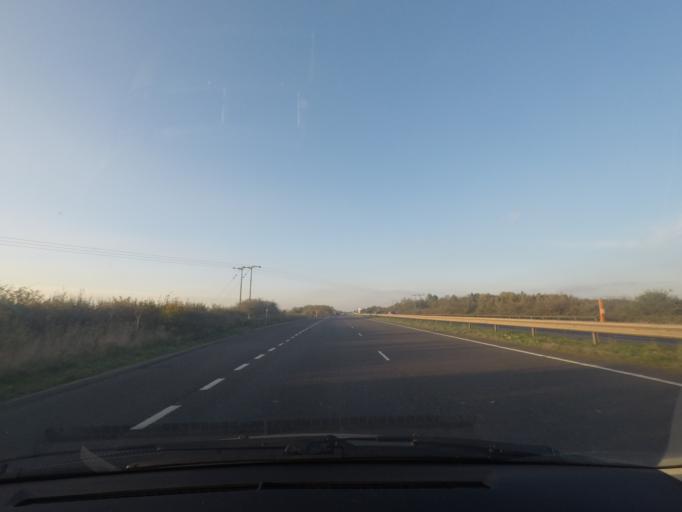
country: GB
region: England
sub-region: North Lincolnshire
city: Barnetby le Wold
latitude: 53.5962
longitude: -0.4195
